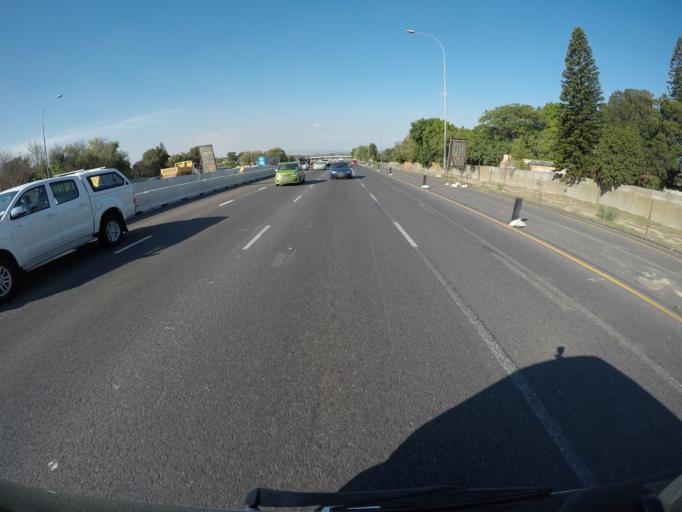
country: ZA
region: Western Cape
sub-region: City of Cape Town
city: Kraaifontein
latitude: -33.8796
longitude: 18.6530
